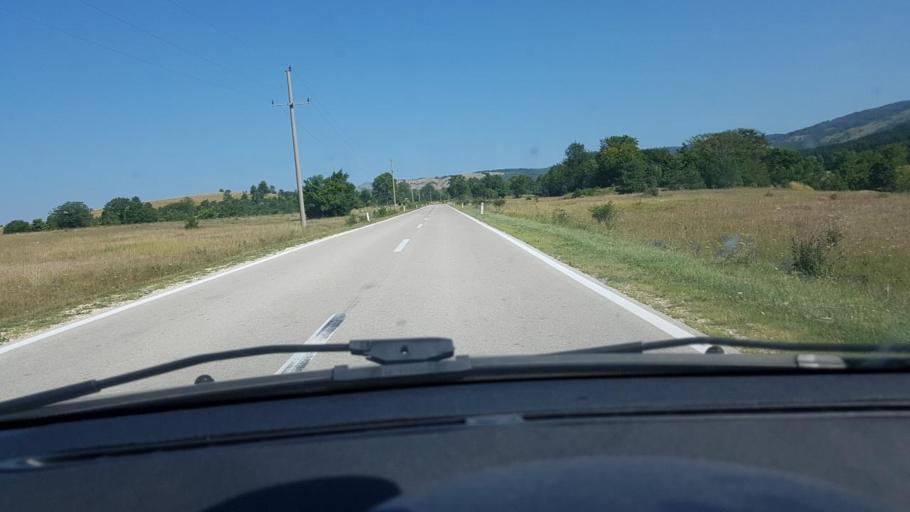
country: BA
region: Federation of Bosnia and Herzegovina
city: Bosansko Grahovo
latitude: 44.1013
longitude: 16.5518
